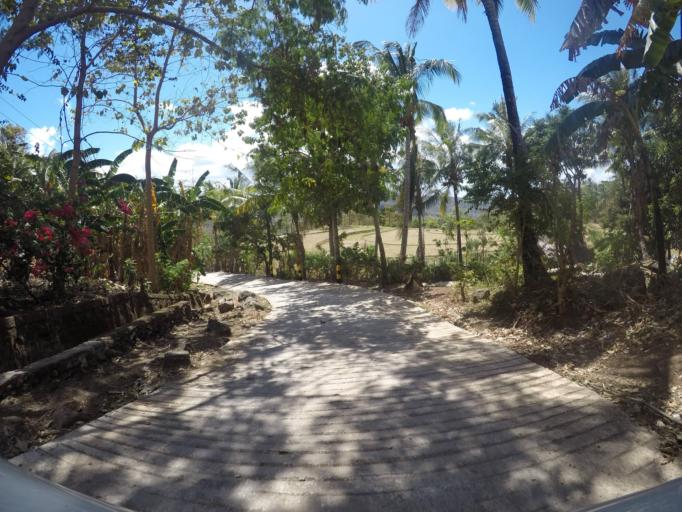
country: TL
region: Lautem
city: Lospalos
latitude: -8.5362
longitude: 126.7991
